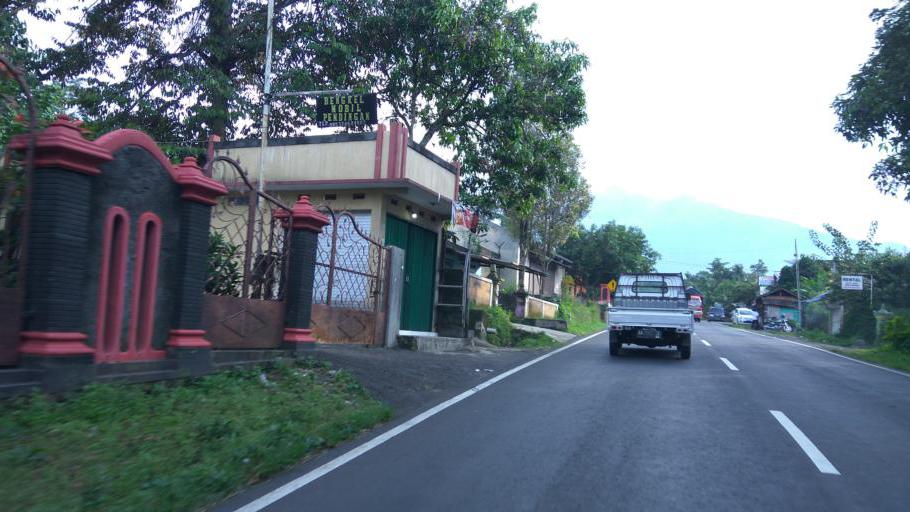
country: ID
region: Central Java
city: Salatiga
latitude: -7.3623
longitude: 110.4746
